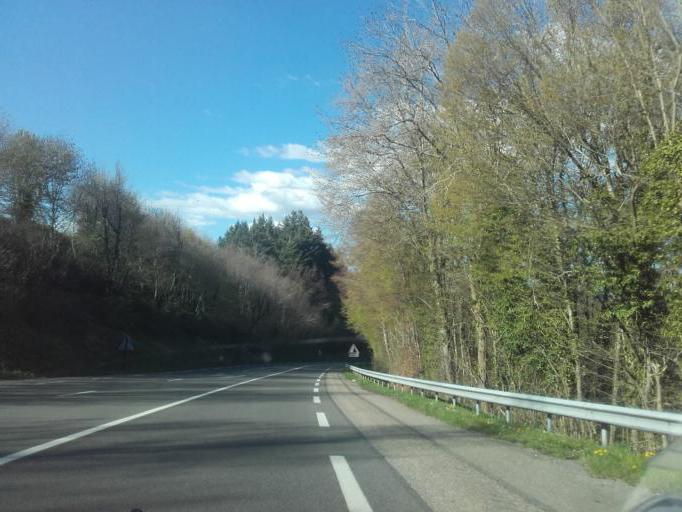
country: FR
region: Rhone-Alpes
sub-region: Departement de l'Isere
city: Nivolas-Vermelle
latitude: 45.5217
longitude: 5.3035
